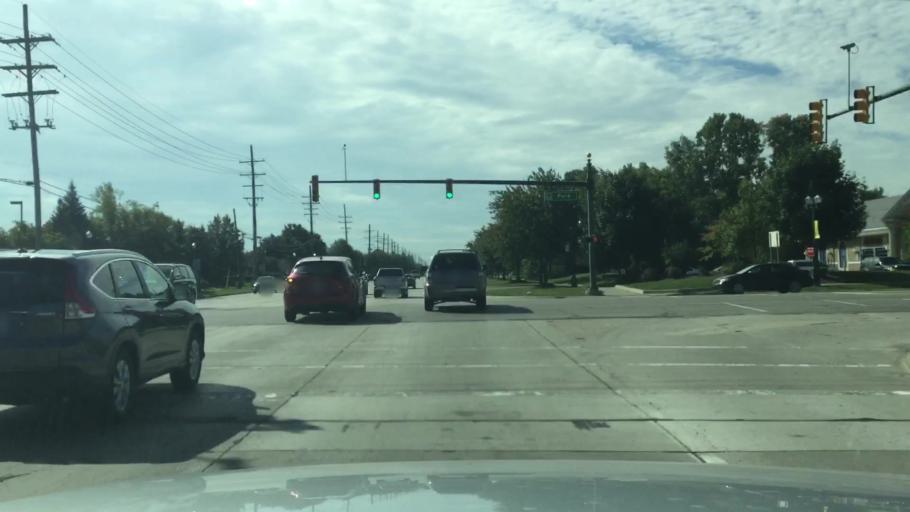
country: US
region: Michigan
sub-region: Wayne County
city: Canton
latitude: 42.3222
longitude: -83.4880
